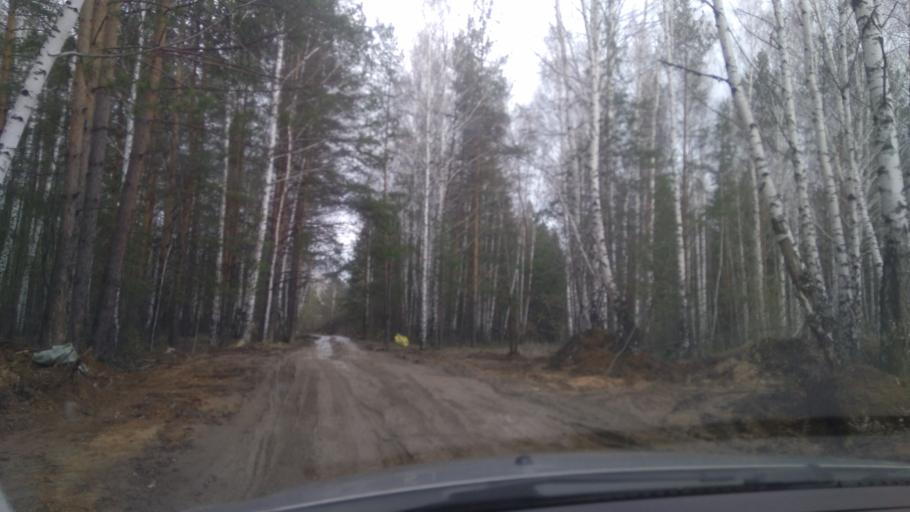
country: RU
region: Sverdlovsk
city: Verkhnyaya Pyshma
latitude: 56.9239
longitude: 60.5973
